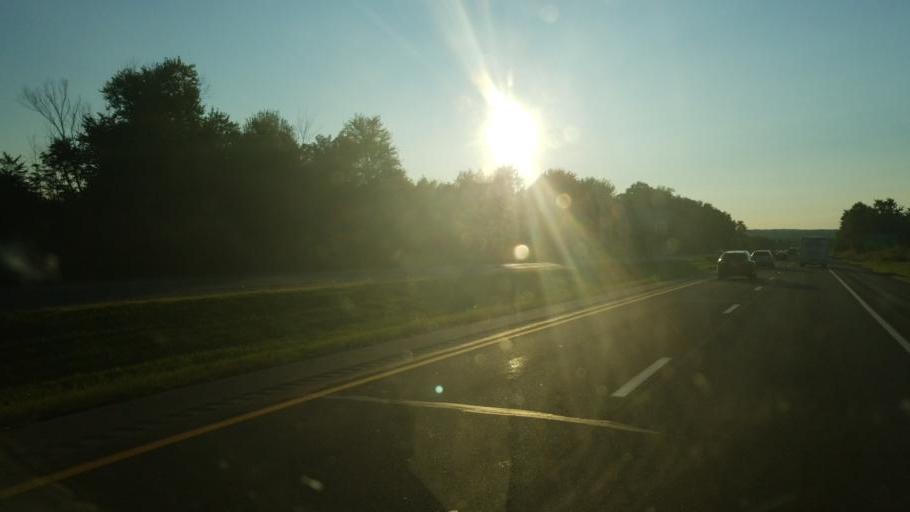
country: US
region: Ohio
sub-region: Mahoning County
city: Boardman
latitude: 40.9726
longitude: -80.6643
